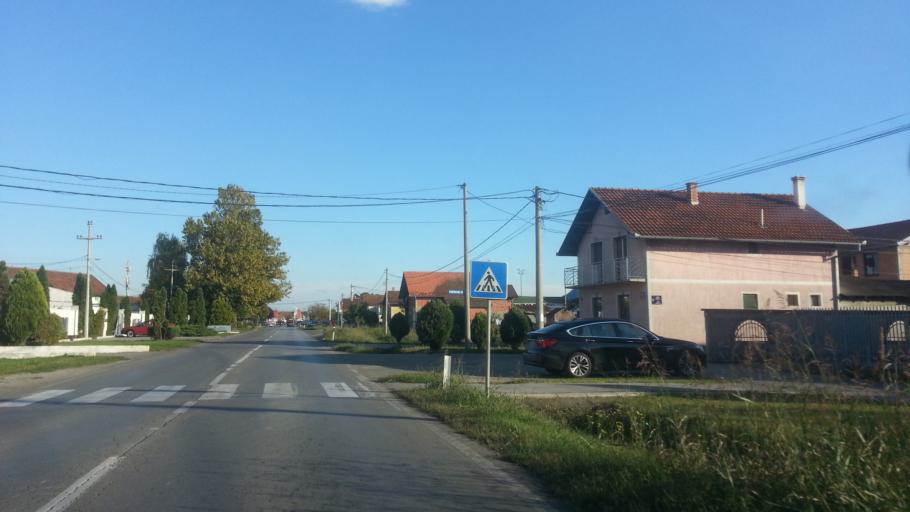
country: RS
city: Novi Banovci
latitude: 44.9145
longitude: 20.2588
